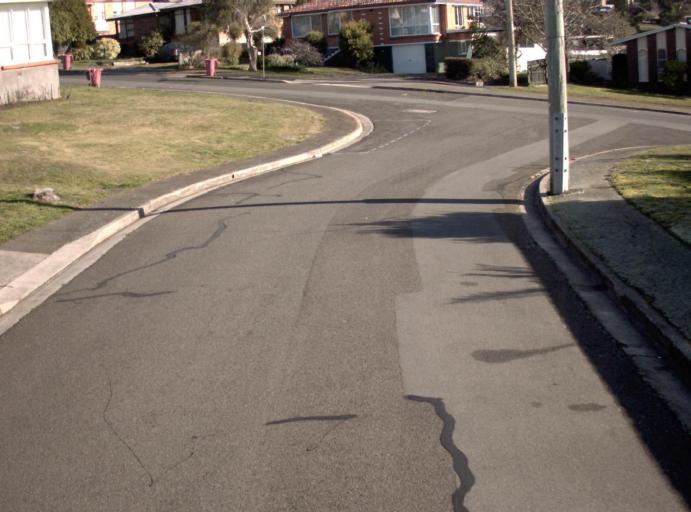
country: AU
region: Tasmania
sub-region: Launceston
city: Summerhill
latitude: -41.4657
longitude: 147.1205
